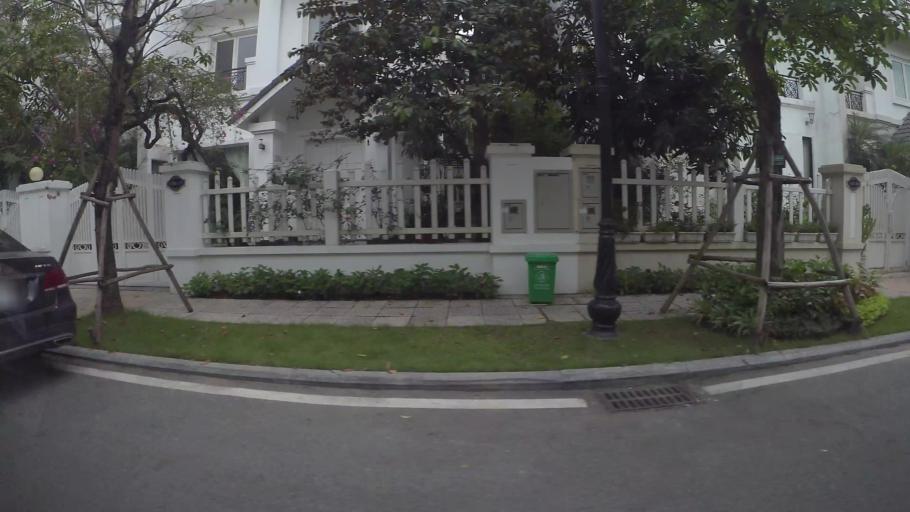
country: VN
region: Ha Noi
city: Trau Quy
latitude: 21.0462
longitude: 105.9128
